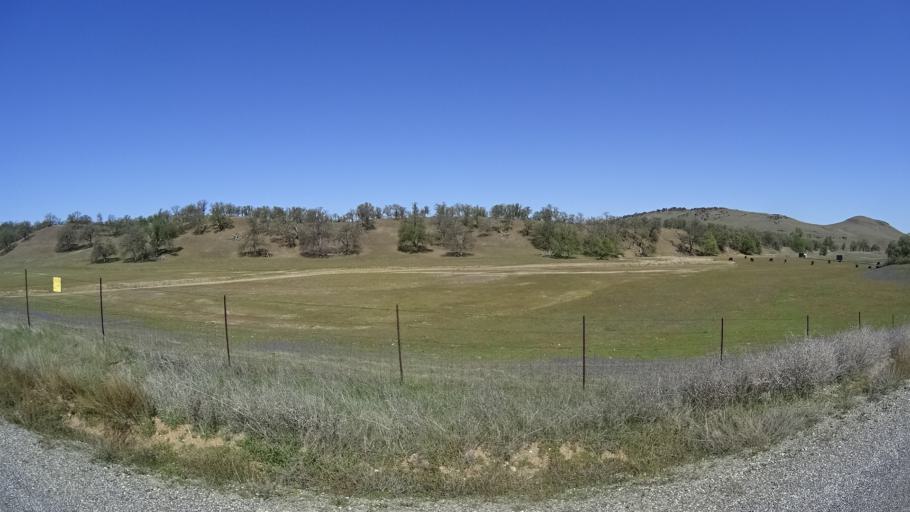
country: US
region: California
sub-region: Glenn County
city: Orland
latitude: 39.7575
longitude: -122.3479
